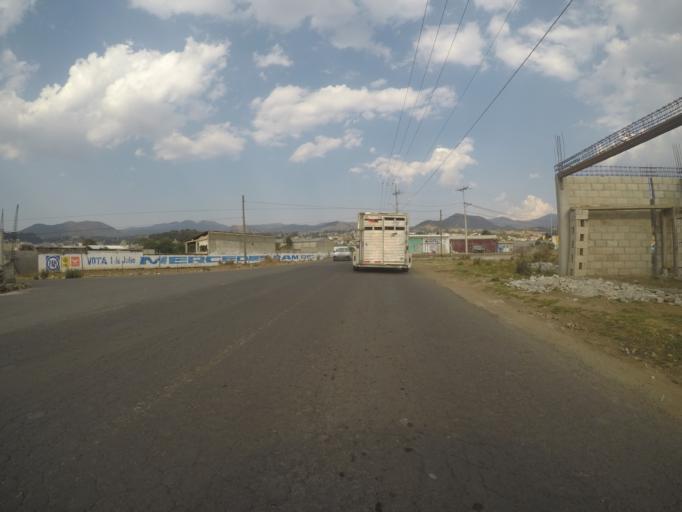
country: MX
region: Mexico
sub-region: Xalatlaco
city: Techichili
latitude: 19.1717
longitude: -99.4148
